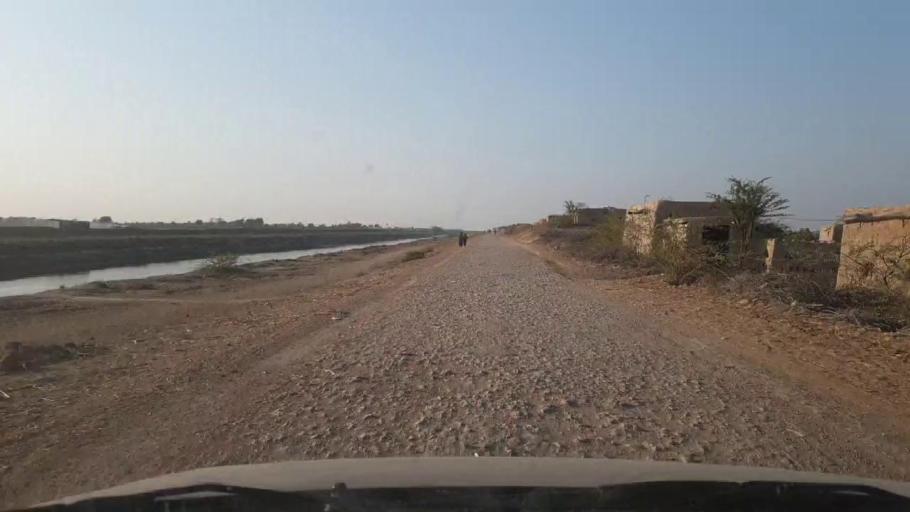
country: PK
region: Sindh
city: Samaro
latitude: 25.2814
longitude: 69.3402
